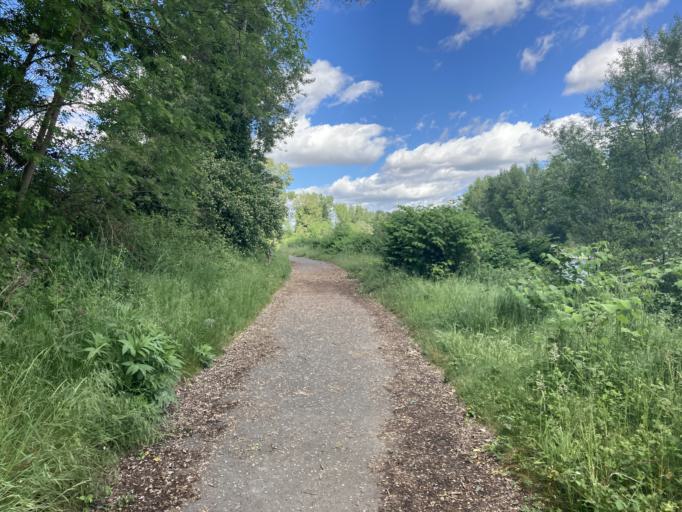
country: FR
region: Aquitaine
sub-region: Departement des Pyrenees-Atlantiques
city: Arbus
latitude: 43.3403
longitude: -0.5015
